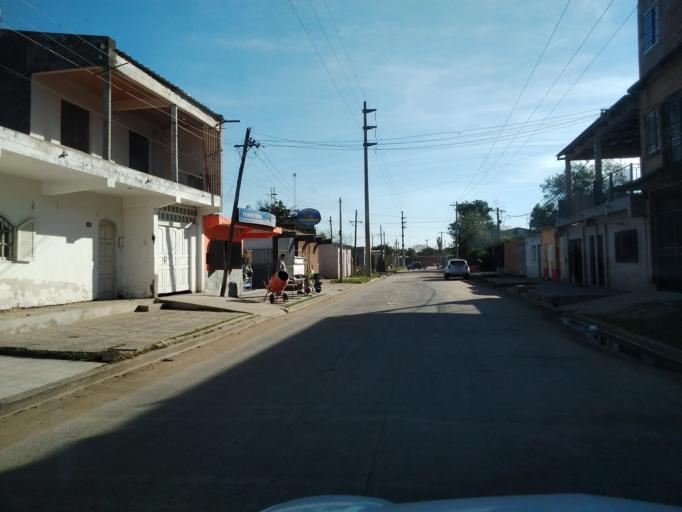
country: AR
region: Corrientes
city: Corrientes
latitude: -27.4978
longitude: -58.8397
